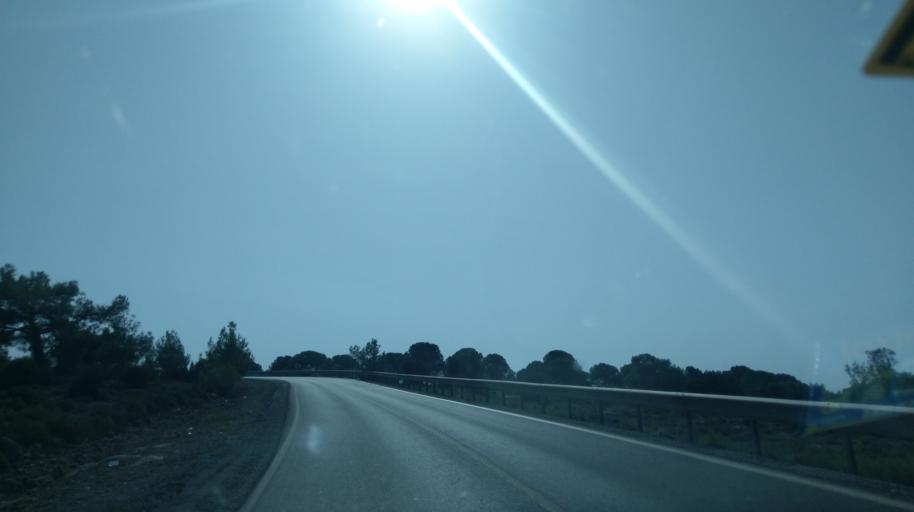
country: CY
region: Lefkosia
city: Morfou
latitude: 35.2529
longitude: 33.0325
